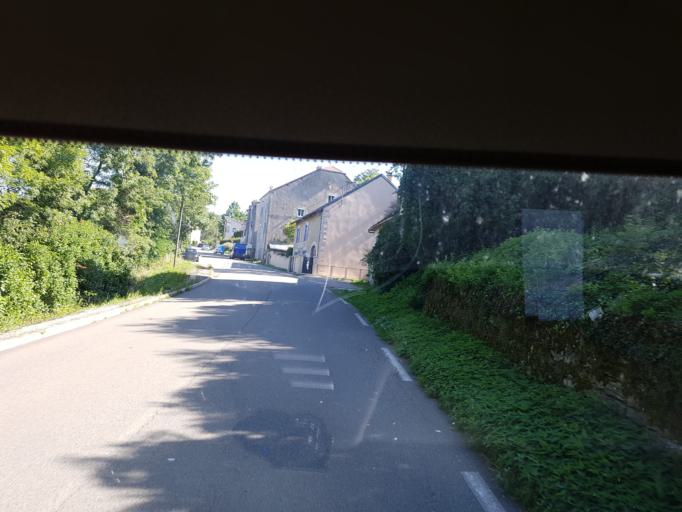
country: FR
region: Franche-Comte
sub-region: Departement du Jura
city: Perrigny
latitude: 46.6950
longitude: 5.5985
